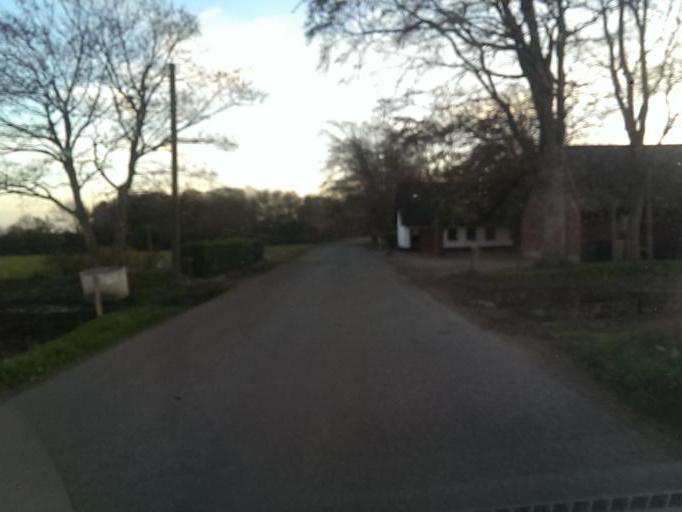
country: DK
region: South Denmark
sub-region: Esbjerg Kommune
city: Tjaereborg
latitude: 55.4741
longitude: 8.6159
